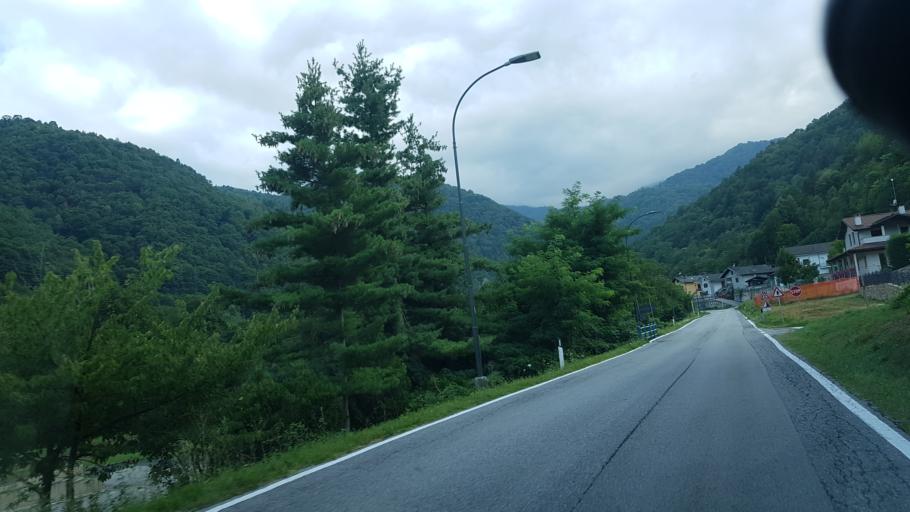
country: IT
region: Piedmont
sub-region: Provincia di Cuneo
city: Brossasco
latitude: 44.5647
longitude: 7.3521
